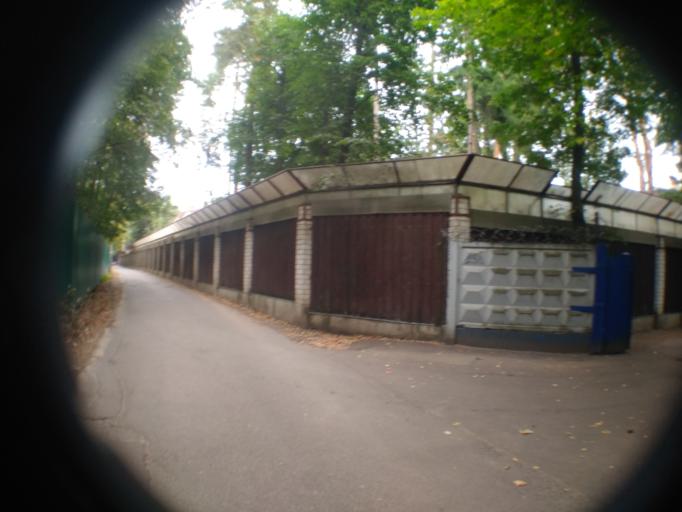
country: RU
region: Moskovskaya
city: Zhukovskiy
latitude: 55.5919
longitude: 38.1402
